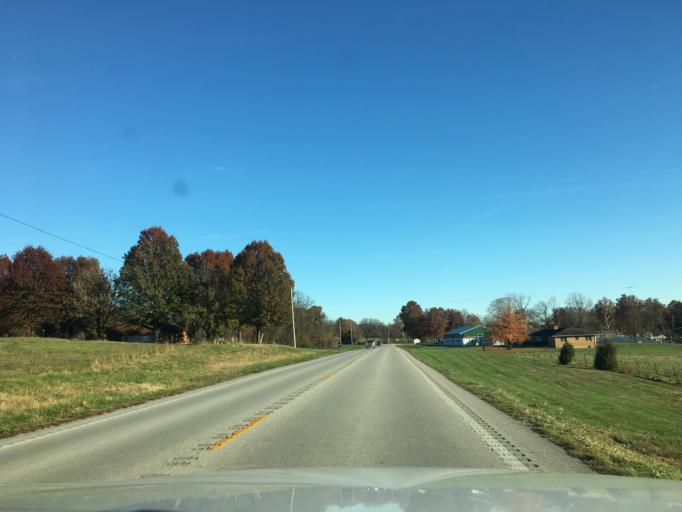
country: US
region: Missouri
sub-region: Franklin County
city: New Haven
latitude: 38.6013
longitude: -91.2584
